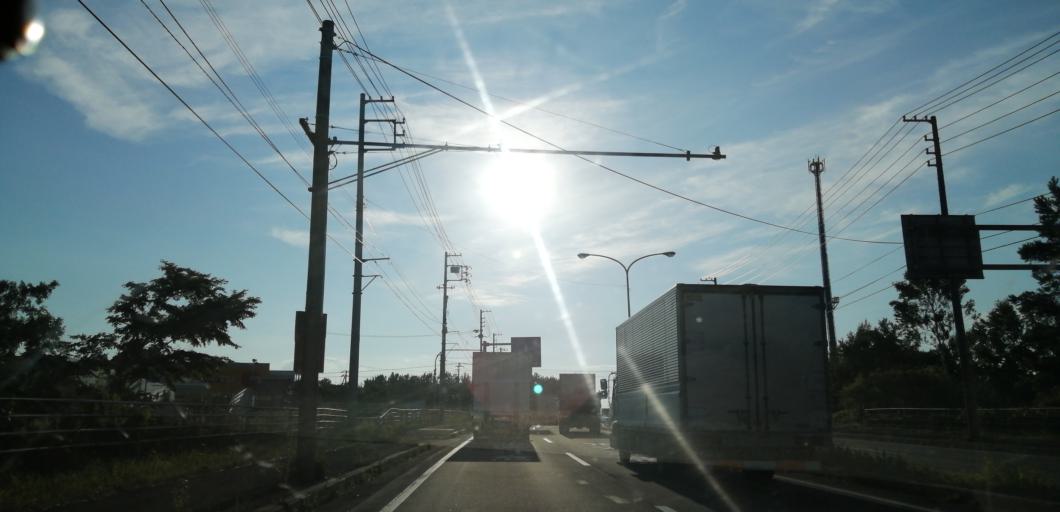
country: JP
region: Hokkaido
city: Kitahiroshima
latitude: 42.9971
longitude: 141.5642
